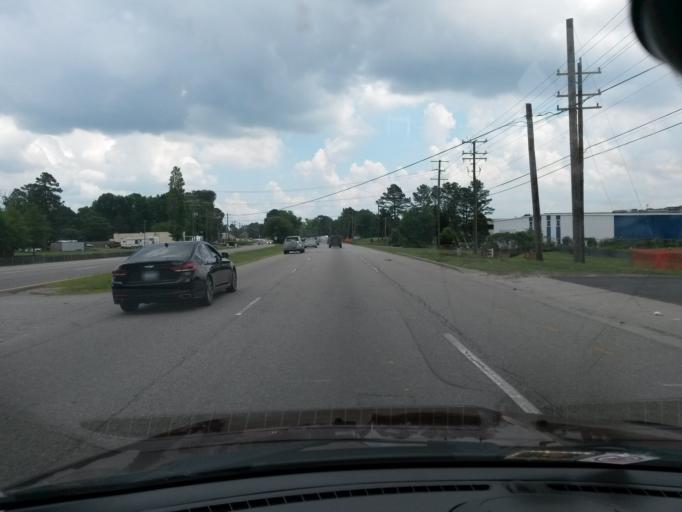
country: US
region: Virginia
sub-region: Chesterfield County
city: Chester
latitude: 37.3509
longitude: -77.3853
